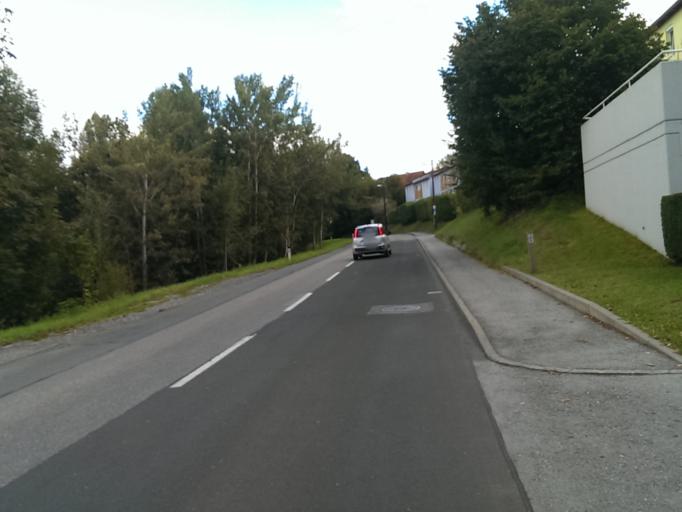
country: AT
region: Styria
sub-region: Politischer Bezirk Graz-Umgebung
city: Hart bei Graz
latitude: 47.0684
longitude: 15.5053
